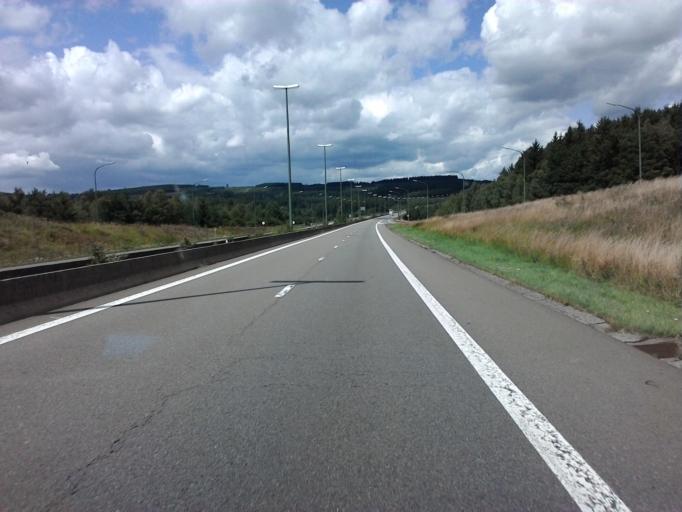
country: BE
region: Wallonia
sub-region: Province du Luxembourg
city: Manhay
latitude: 50.3083
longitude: 5.7141
